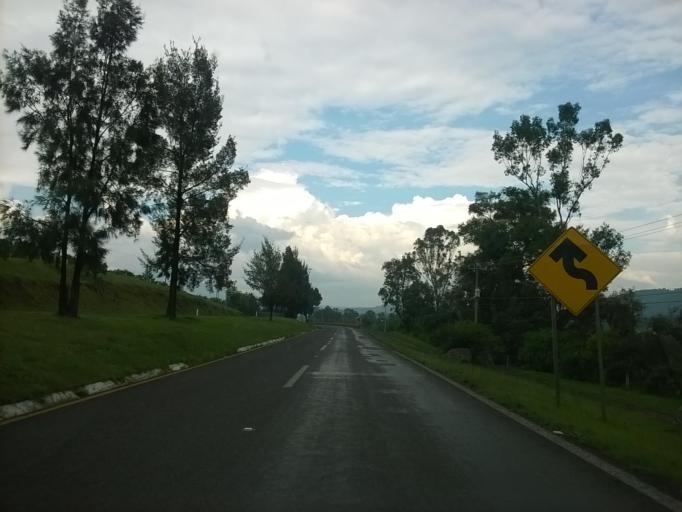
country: MX
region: Michoacan
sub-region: Huiramba
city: El Pedregal
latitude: 19.5309
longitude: -101.4782
